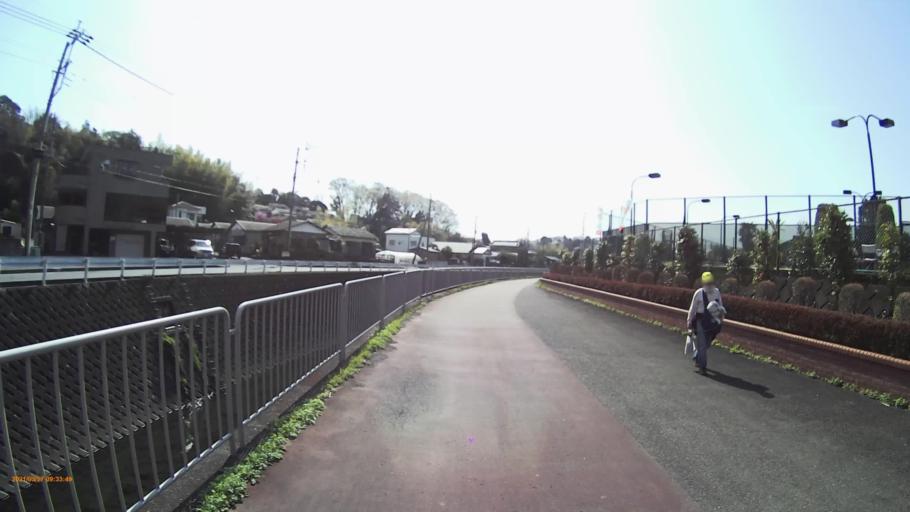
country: JP
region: Kanagawa
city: Atsugi
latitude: 35.4395
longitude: 139.4123
